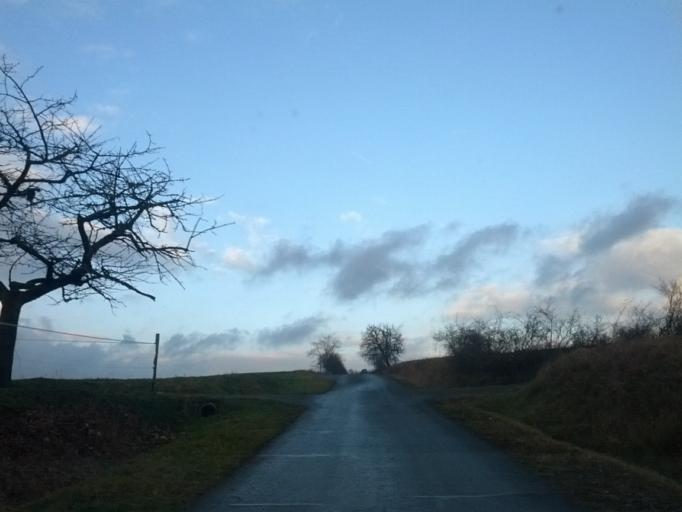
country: DE
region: Thuringia
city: Bischofroda
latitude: 51.0475
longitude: 10.3939
